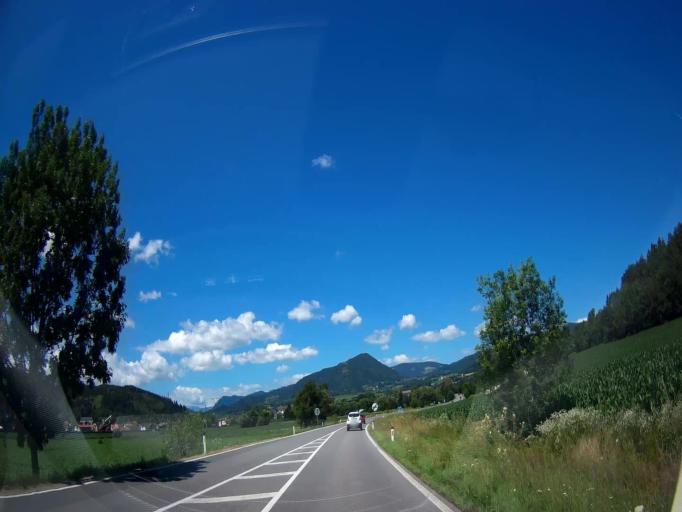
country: AT
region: Carinthia
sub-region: Politischer Bezirk Sankt Veit an der Glan
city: Sankt Veit an der Glan
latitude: 46.7634
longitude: 14.3871
